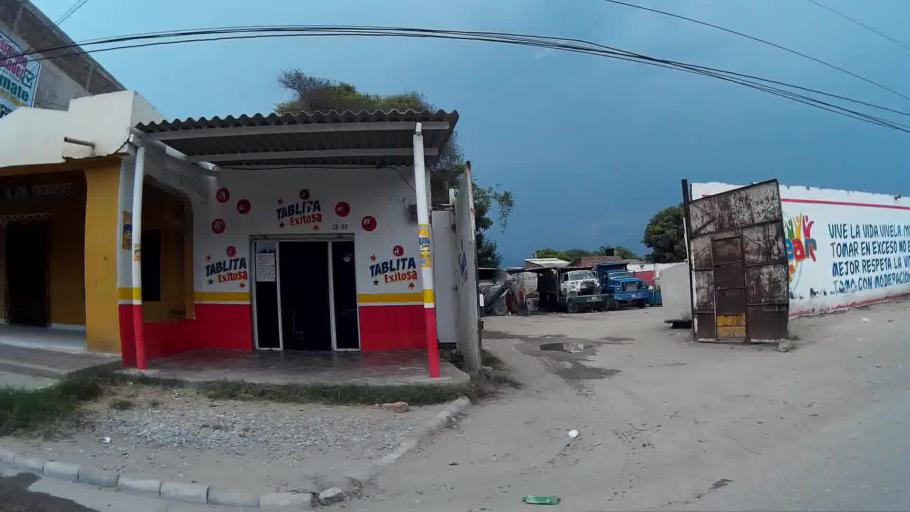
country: CO
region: Magdalena
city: Cienaga
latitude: 11.0076
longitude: -74.2443
